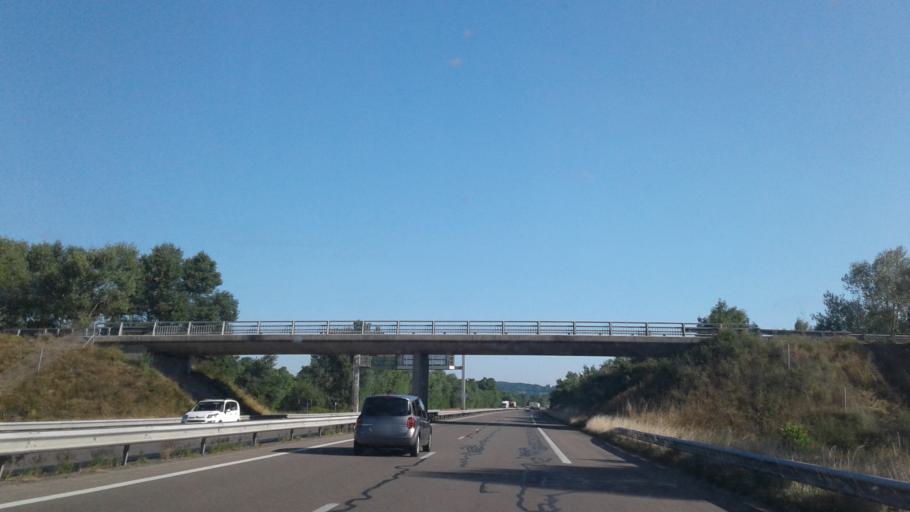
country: FR
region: Rhone-Alpes
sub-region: Departement de l'Ain
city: Priay
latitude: 46.0070
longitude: 5.3123
